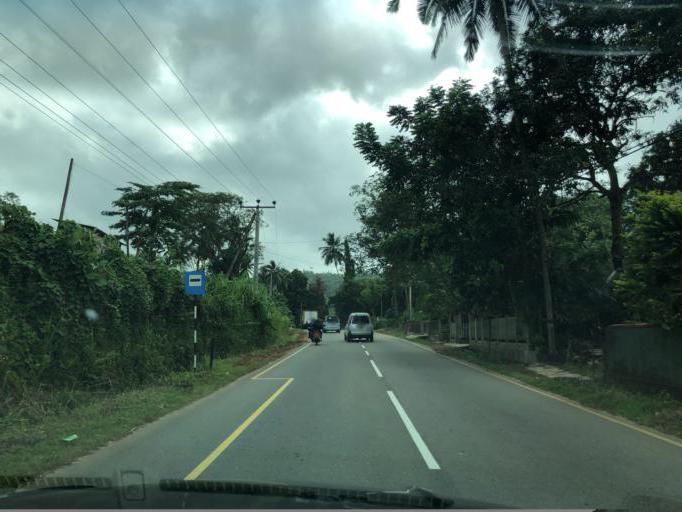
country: LK
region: Western
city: Horana South
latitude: 6.6780
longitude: 80.1550
